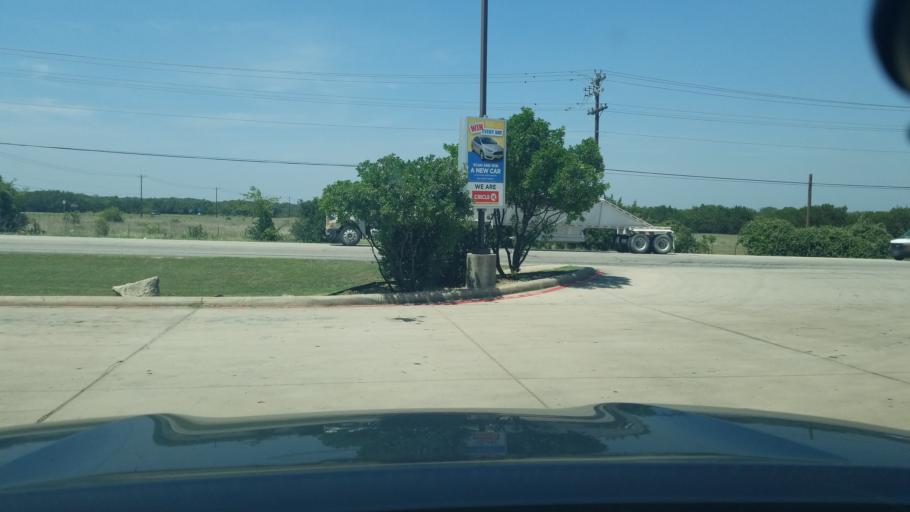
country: US
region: Texas
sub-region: Bexar County
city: Fair Oaks Ranch
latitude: 29.8268
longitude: -98.5720
